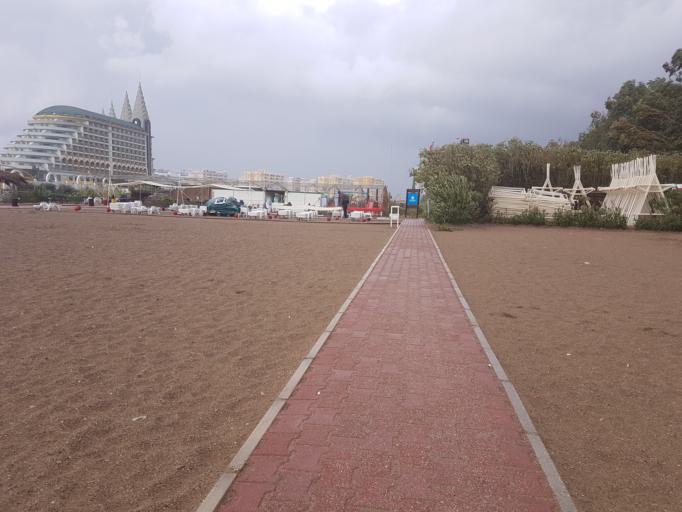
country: TR
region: Antalya
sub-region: Serik
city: Kumkoey
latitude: 36.8529
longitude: 30.8752
